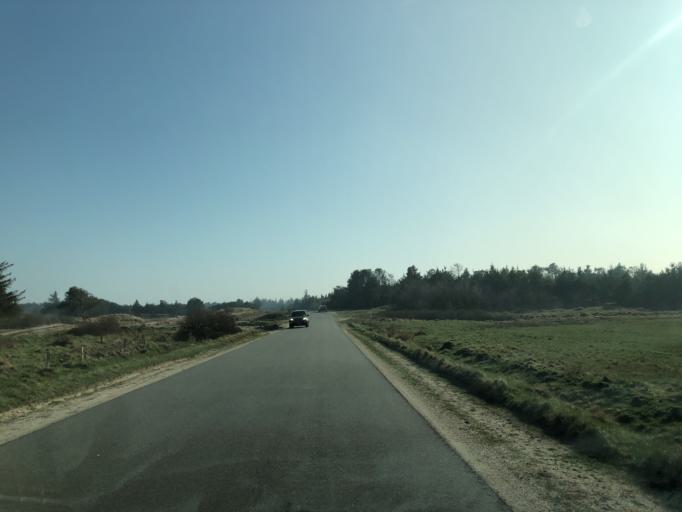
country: DK
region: South Denmark
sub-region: Varde Kommune
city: Oksbol
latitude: 55.6391
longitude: 8.1748
